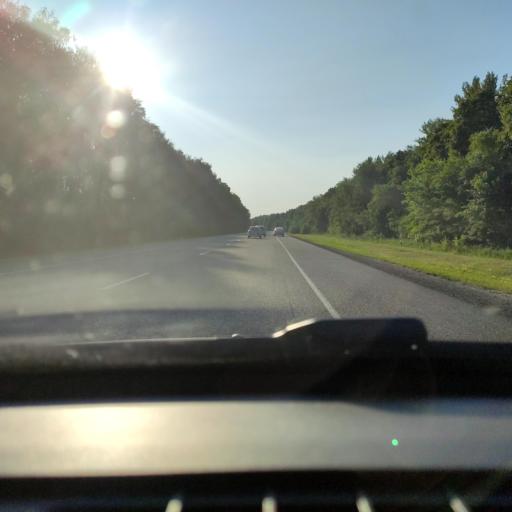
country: RU
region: Voronezj
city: Kashirskoye
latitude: 51.4816
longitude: 39.6624
